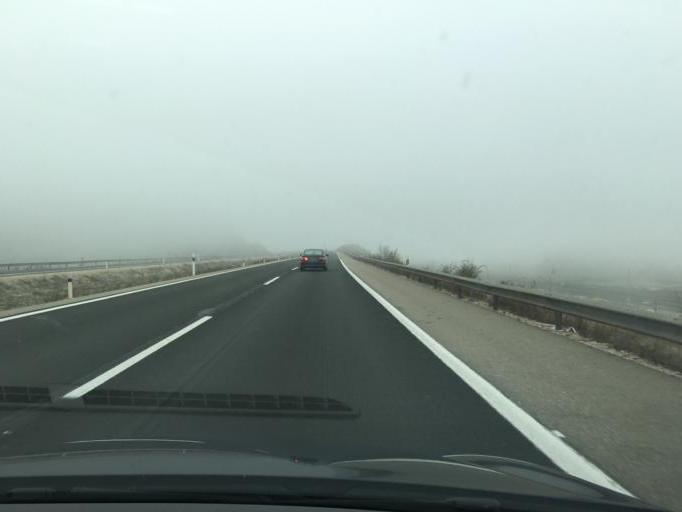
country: ES
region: Castille and Leon
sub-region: Provincia de Burgos
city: Pancorbo
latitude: 42.6226
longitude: -3.1312
